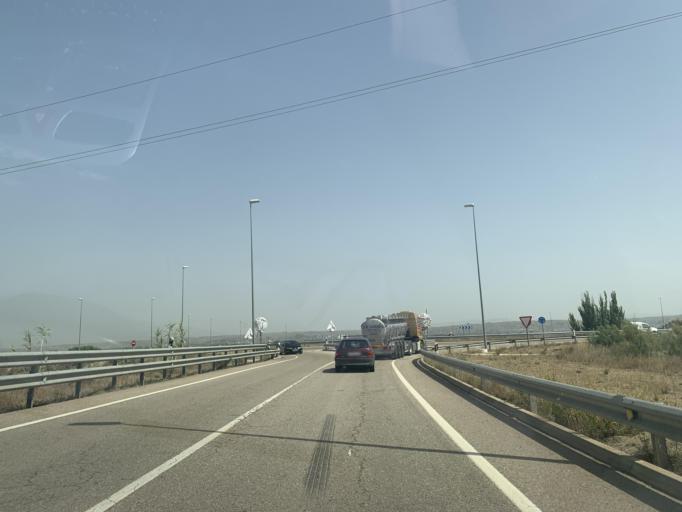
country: ES
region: Aragon
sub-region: Provincia de Zaragoza
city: El Burgo de Ebro
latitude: 41.5437
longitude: -0.6964
